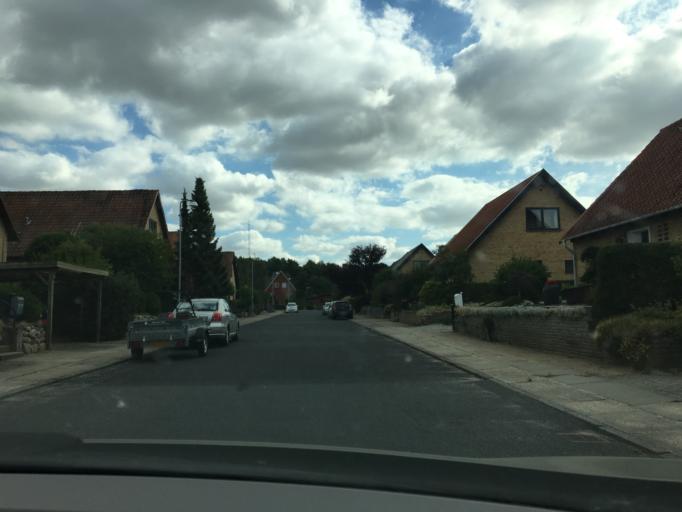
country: DK
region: South Denmark
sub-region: Odense Kommune
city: Odense
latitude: 55.3949
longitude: 10.3290
